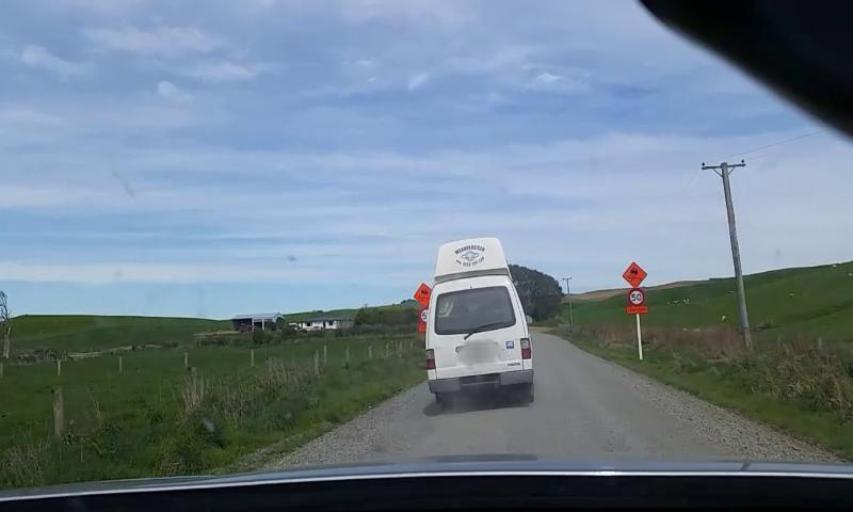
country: NZ
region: Otago
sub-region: Clutha District
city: Papatowai
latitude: -46.6260
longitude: 169.0010
